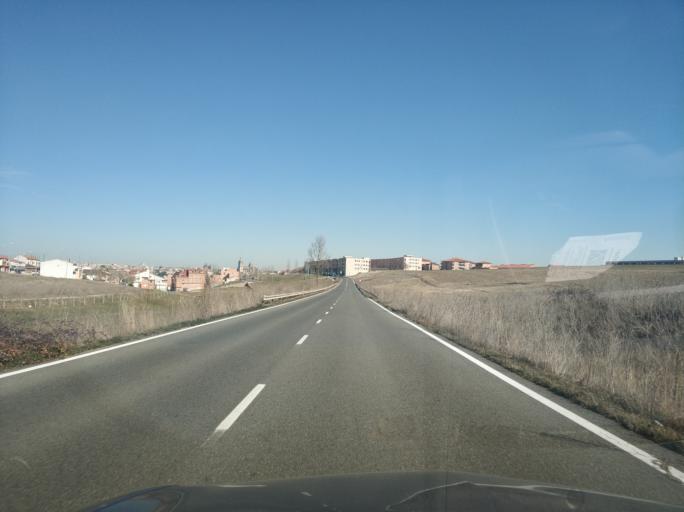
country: ES
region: Castille and Leon
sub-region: Provincia de Salamanca
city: Aldeatejada
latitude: 40.9471
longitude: -5.6897
